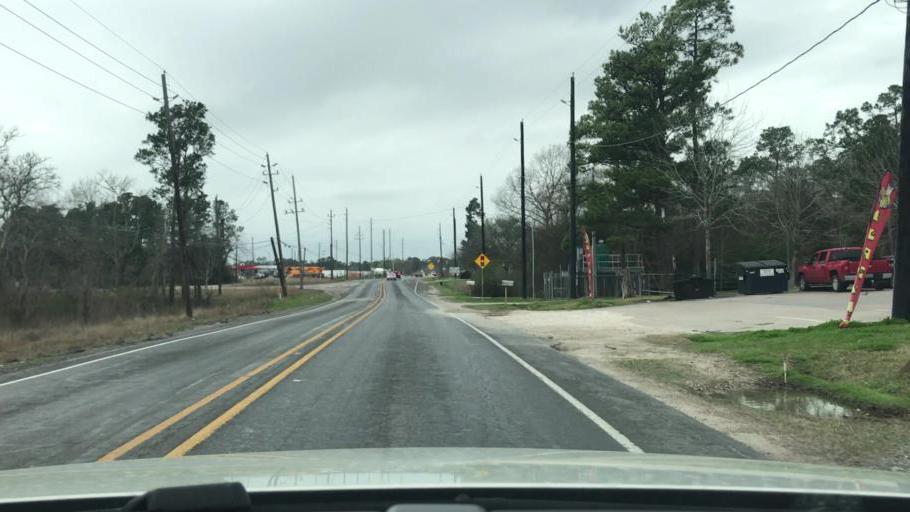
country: US
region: Texas
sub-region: Harris County
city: Baytown
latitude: 29.7733
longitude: -94.9110
